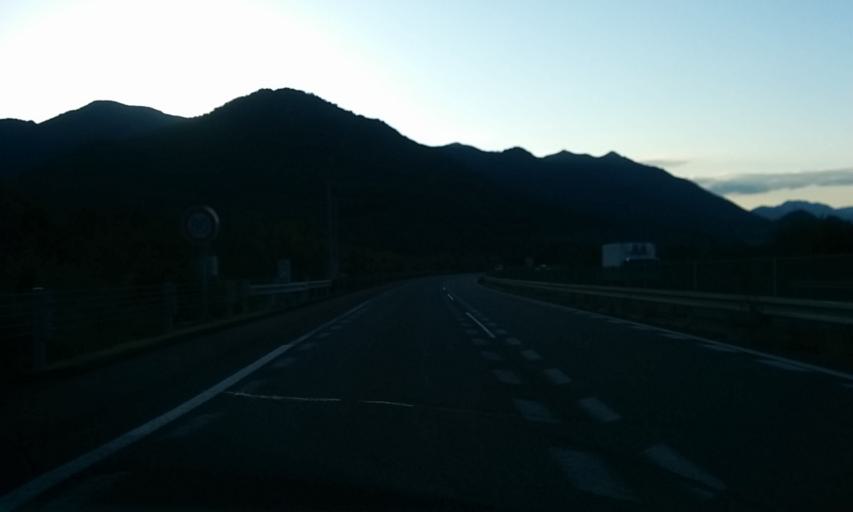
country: JP
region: Hyogo
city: Sasayama
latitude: 35.1407
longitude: 135.1331
